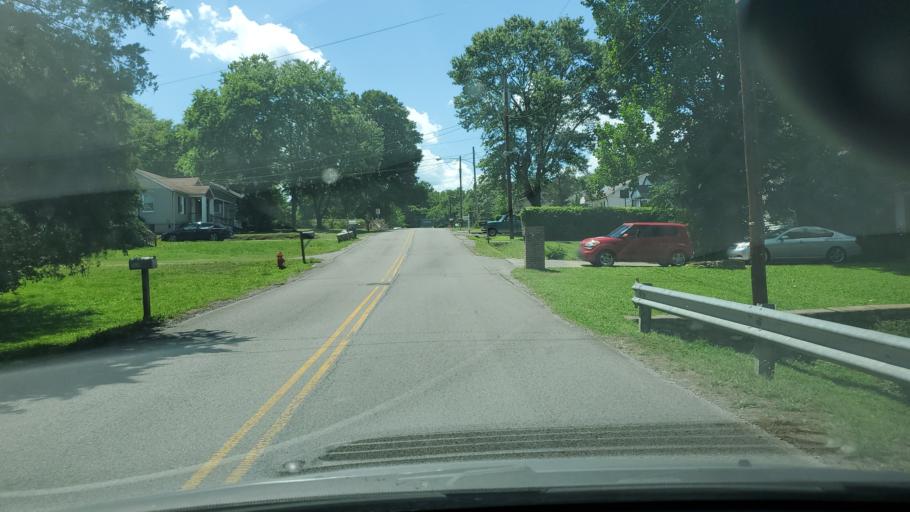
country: US
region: Tennessee
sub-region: Davidson County
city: Nashville
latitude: 36.2008
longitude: -86.7566
